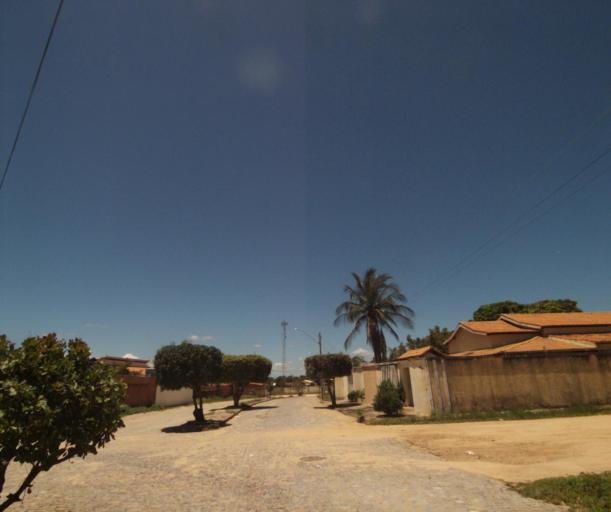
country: BR
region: Bahia
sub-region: Carinhanha
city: Carinhanha
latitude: -14.3073
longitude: -43.7697
